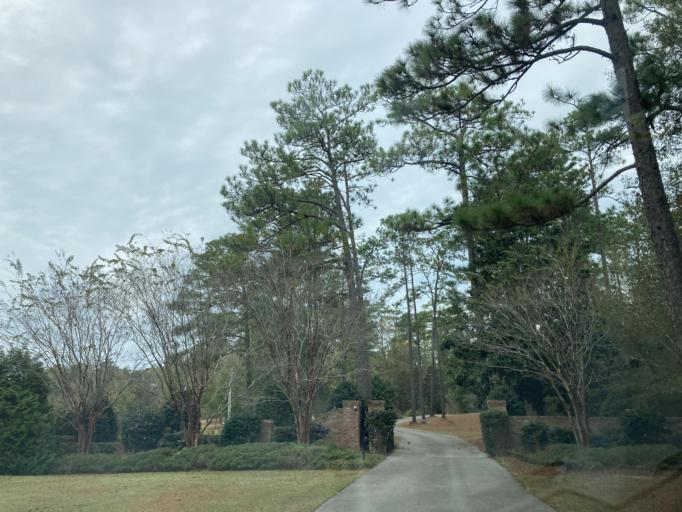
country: US
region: Mississippi
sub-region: Lamar County
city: West Hattiesburg
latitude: 31.3222
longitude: -89.3899
